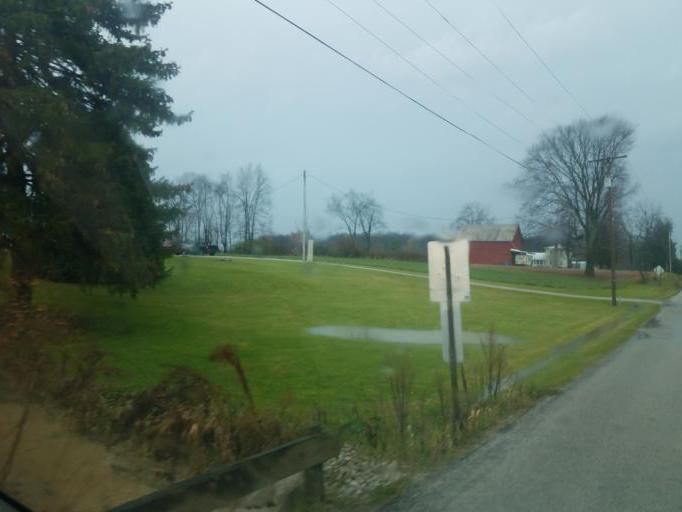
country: US
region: Ohio
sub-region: Morrow County
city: Cardington
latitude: 40.5018
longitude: -82.8727
